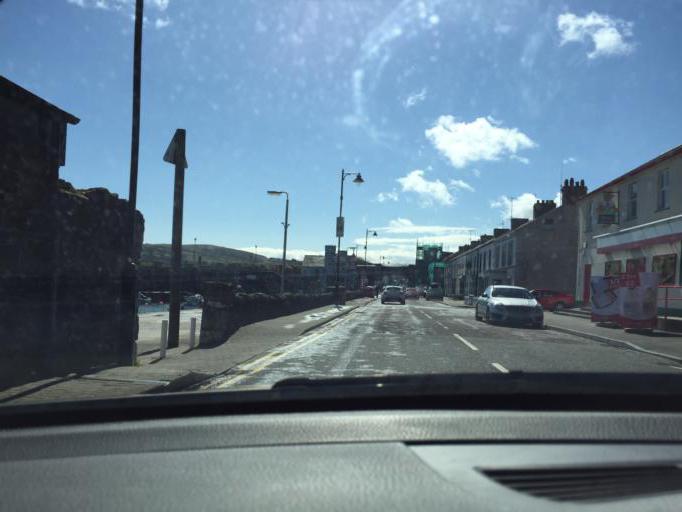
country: GB
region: Northern Ireland
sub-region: Larne District
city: Carnlough
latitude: 54.9940
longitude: -5.9890
